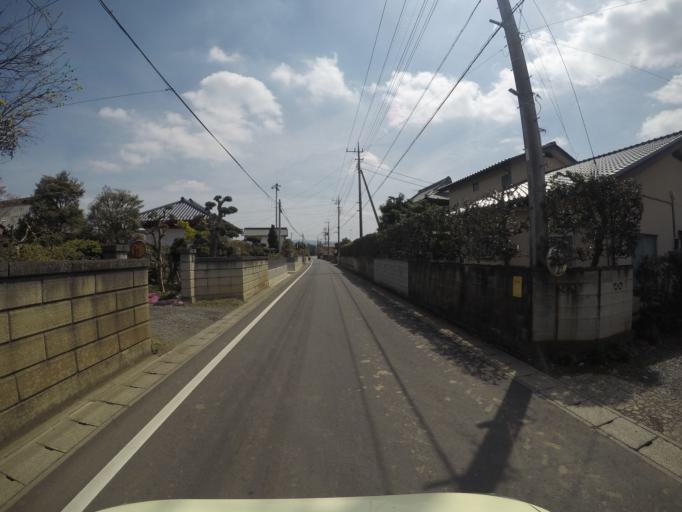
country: JP
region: Ibaraki
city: Shimodate
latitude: 36.2722
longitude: 140.0276
